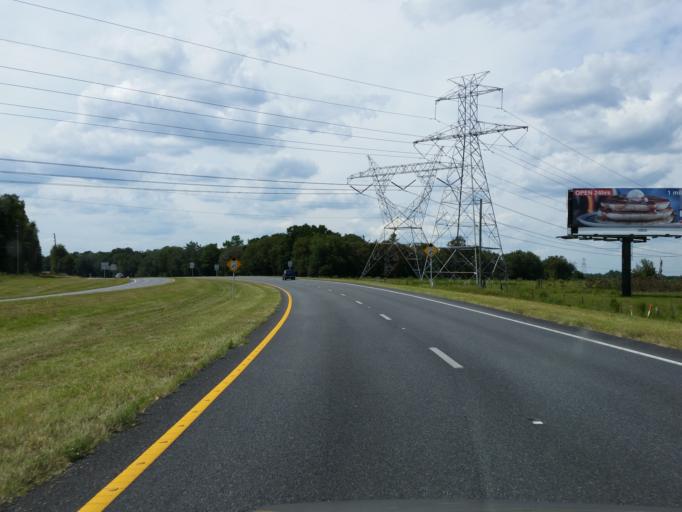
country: US
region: Florida
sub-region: Sumter County
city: Wildwood
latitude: 28.8697
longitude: -82.0823
